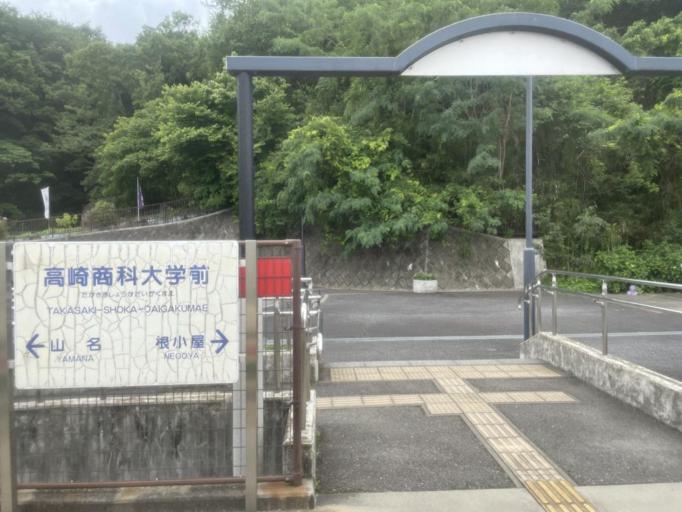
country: JP
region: Gunma
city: Takasaki
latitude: 36.2843
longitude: 139.0296
